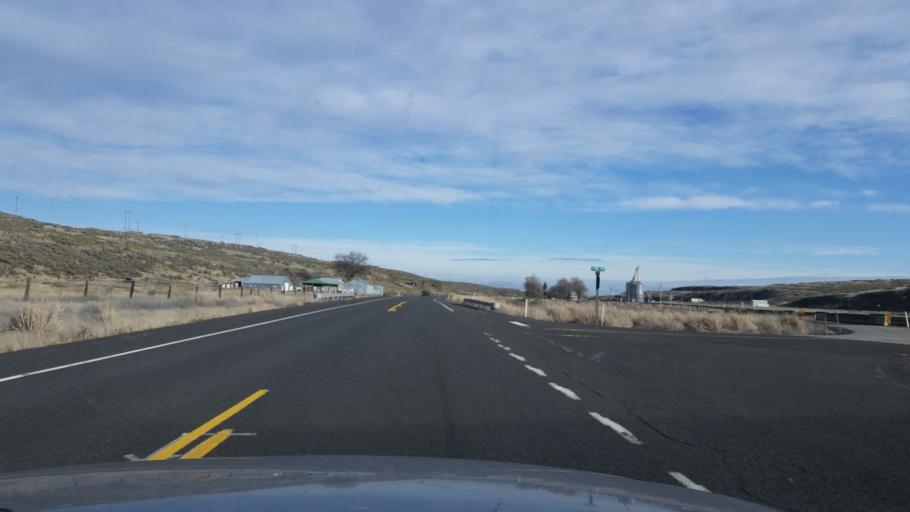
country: US
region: Washington
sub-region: Adams County
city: Ritzville
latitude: 47.3580
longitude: -118.4946
